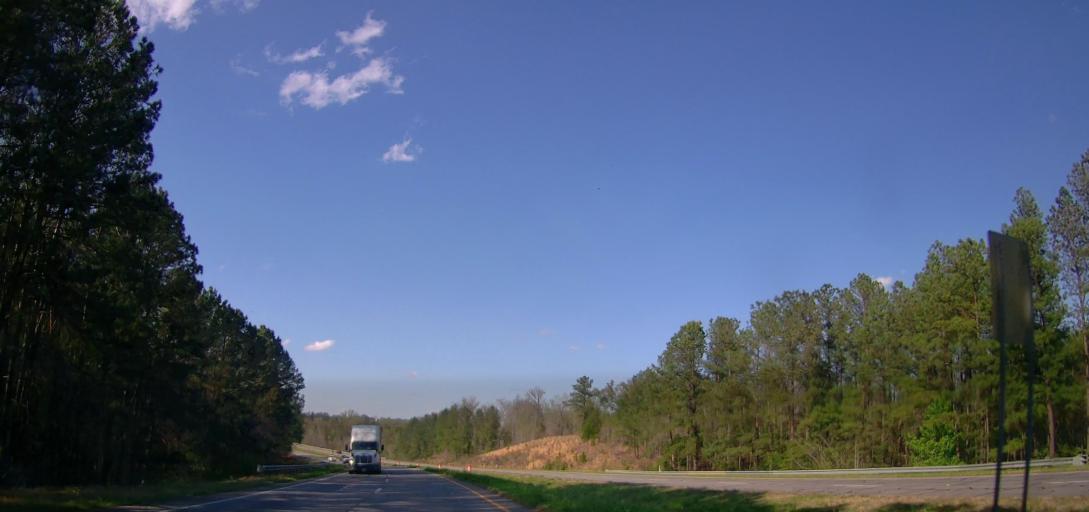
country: US
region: Georgia
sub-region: Baldwin County
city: Milledgeville
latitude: 33.0673
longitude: -83.2491
